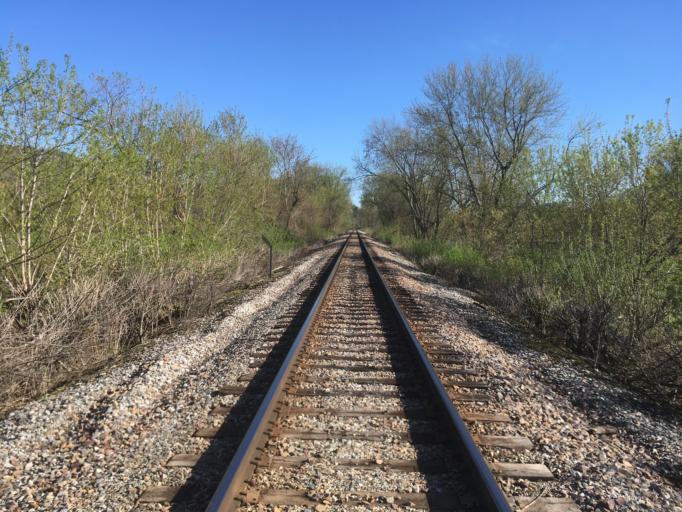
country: US
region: Vermont
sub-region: Rutland County
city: West Rutland
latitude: 43.6429
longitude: -73.0364
